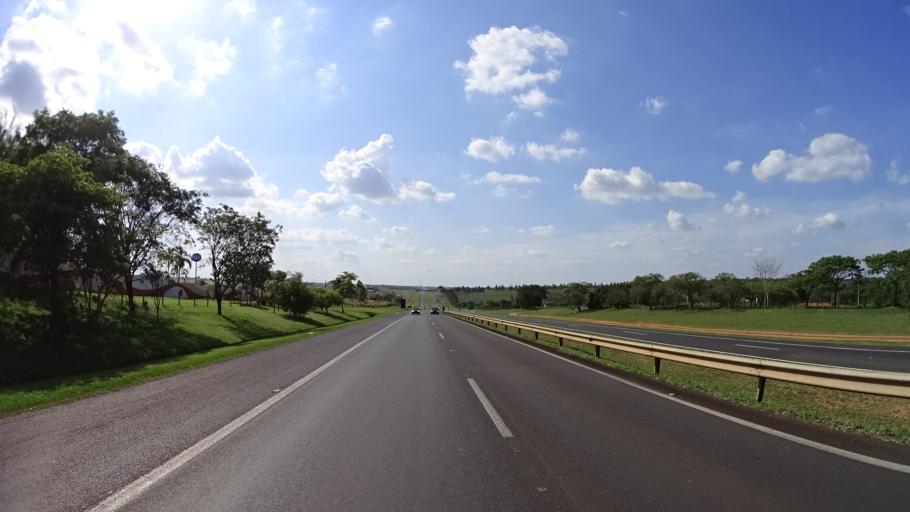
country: BR
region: Sao Paulo
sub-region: Sao Jose Do Rio Preto
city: Sao Jose do Rio Preto
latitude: -20.9156
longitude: -49.2861
